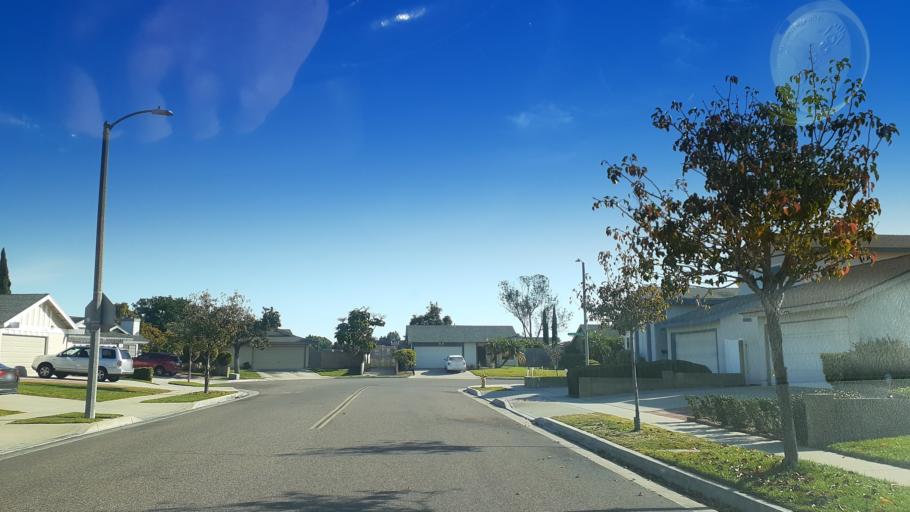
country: US
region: California
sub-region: Los Angeles County
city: Cerritos
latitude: 33.8639
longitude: -118.0691
